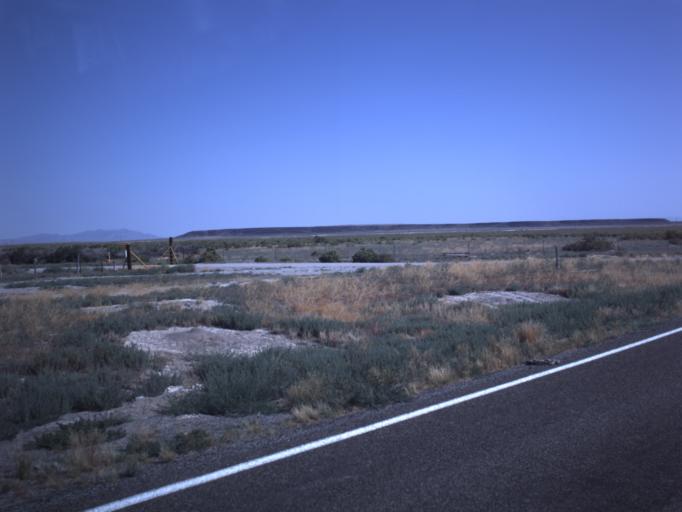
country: US
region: Utah
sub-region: Millard County
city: Delta
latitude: 39.1186
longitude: -112.7395
